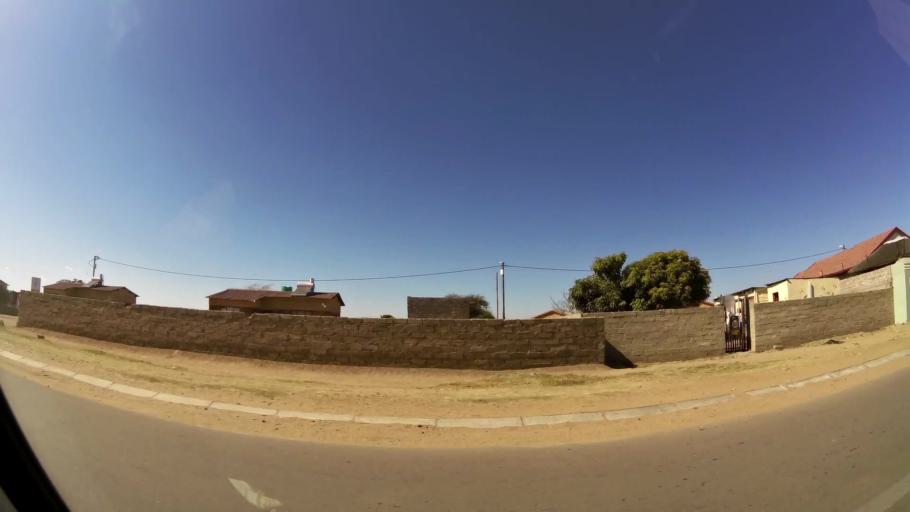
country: ZA
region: Limpopo
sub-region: Capricorn District Municipality
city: Polokwane
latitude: -23.8548
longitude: 29.4133
